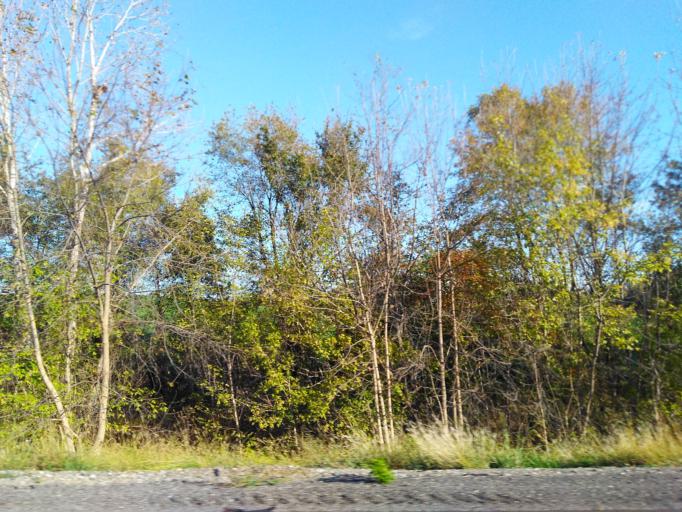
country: US
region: Illinois
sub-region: Madison County
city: Highland
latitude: 38.7866
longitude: -89.6576
